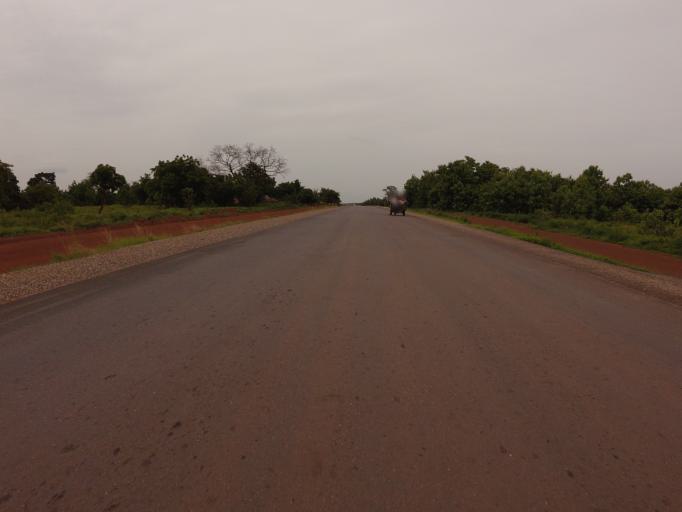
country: GH
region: Northern
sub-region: Yendi
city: Yendi
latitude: 9.3444
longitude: 0.0044
